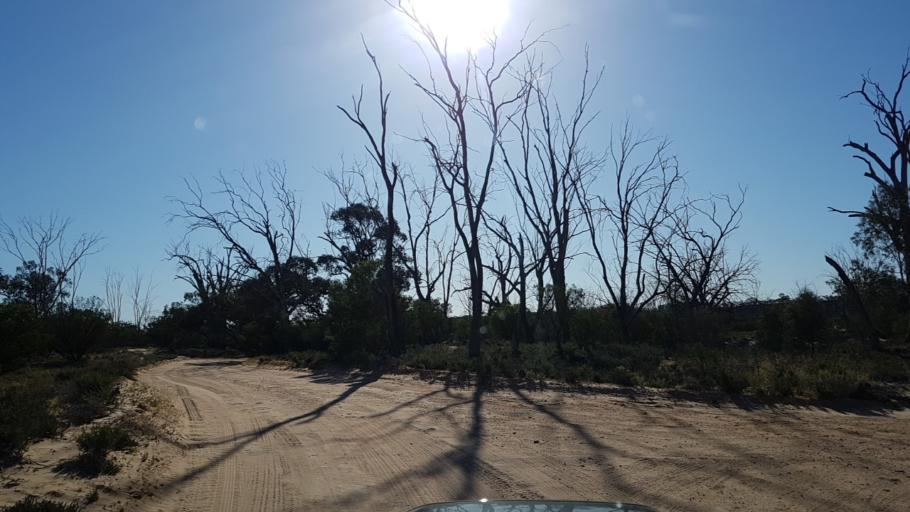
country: AU
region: South Australia
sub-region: Loxton Waikerie
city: Waikerie
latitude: -34.1580
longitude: 140.0268
